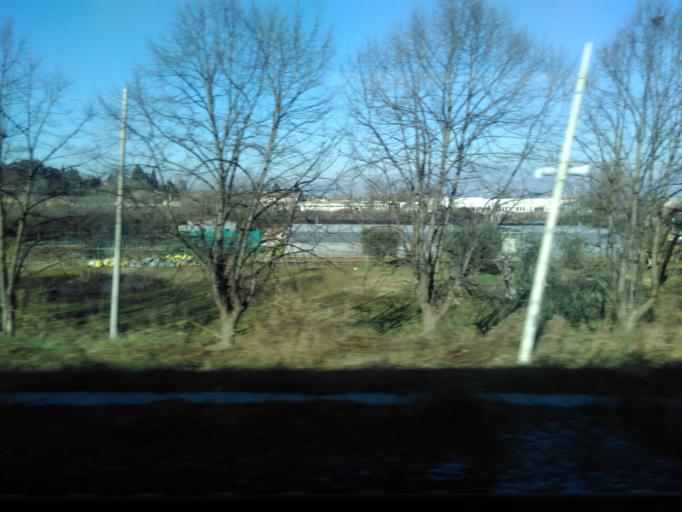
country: IT
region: Veneto
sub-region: Provincia di Verona
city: Sona
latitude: 45.4268
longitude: 10.8464
